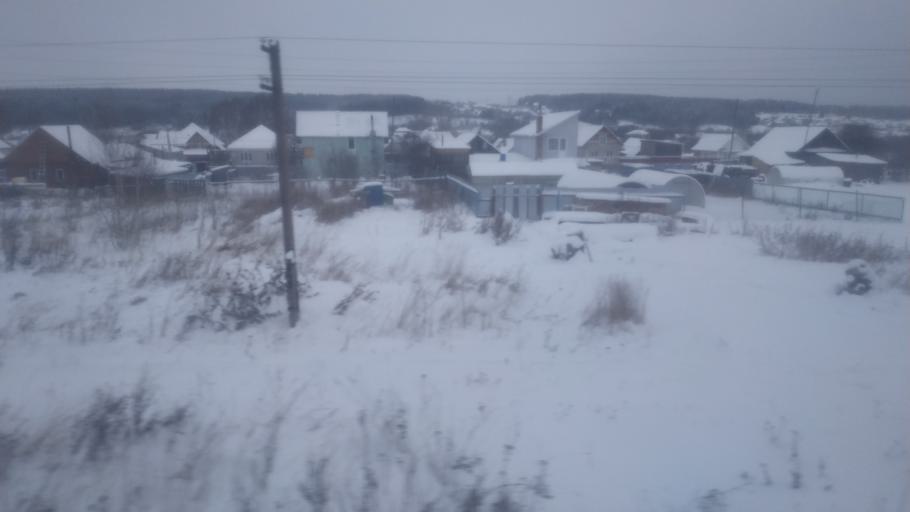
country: RU
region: Udmurtiya
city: Sigayevo
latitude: 56.4524
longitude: 53.7107
